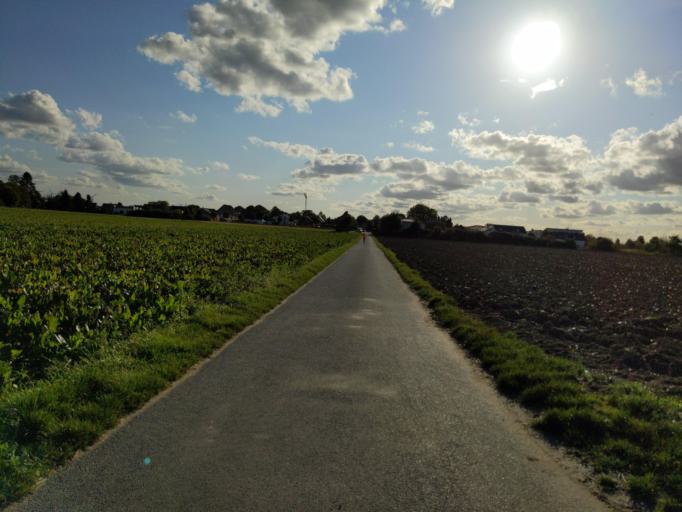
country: DE
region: North Rhine-Westphalia
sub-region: Regierungsbezirk Dusseldorf
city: Kaarst
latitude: 51.2112
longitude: 6.5956
